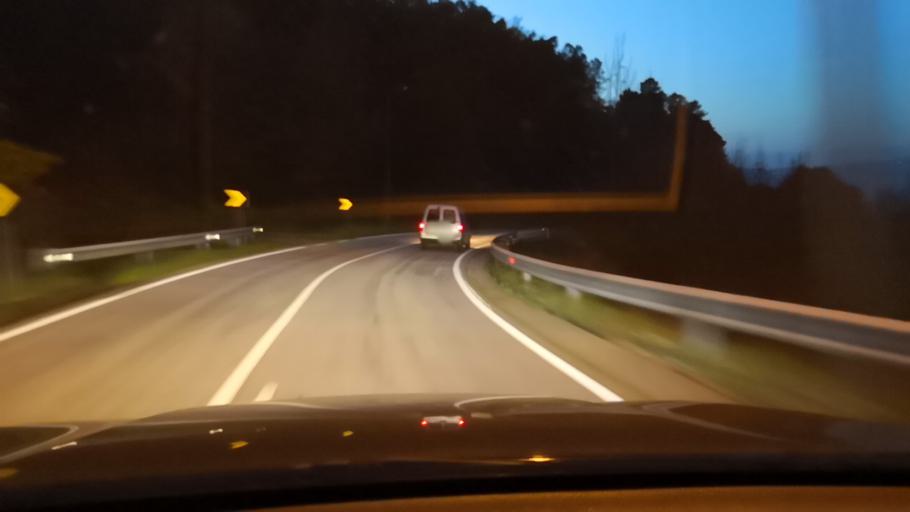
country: PT
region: Porto
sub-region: Baiao
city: Baiao
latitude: 41.2302
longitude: -8.0117
